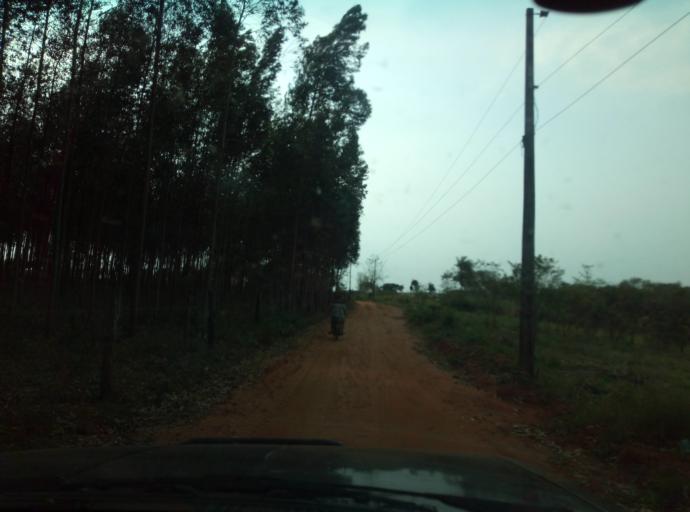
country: PY
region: Caaguazu
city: San Joaquin
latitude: -25.1480
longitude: -56.0963
